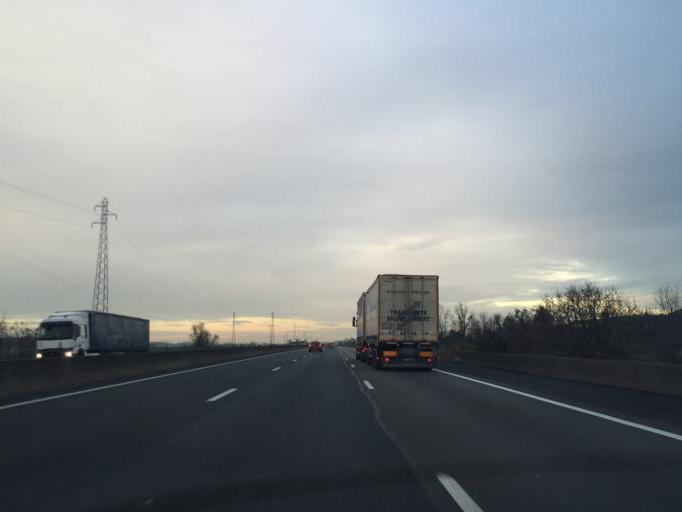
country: FR
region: Bourgogne
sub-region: Departement de Saone-et-Loire
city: La Chapelle-de-Guinchay
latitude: 46.2022
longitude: 4.7803
